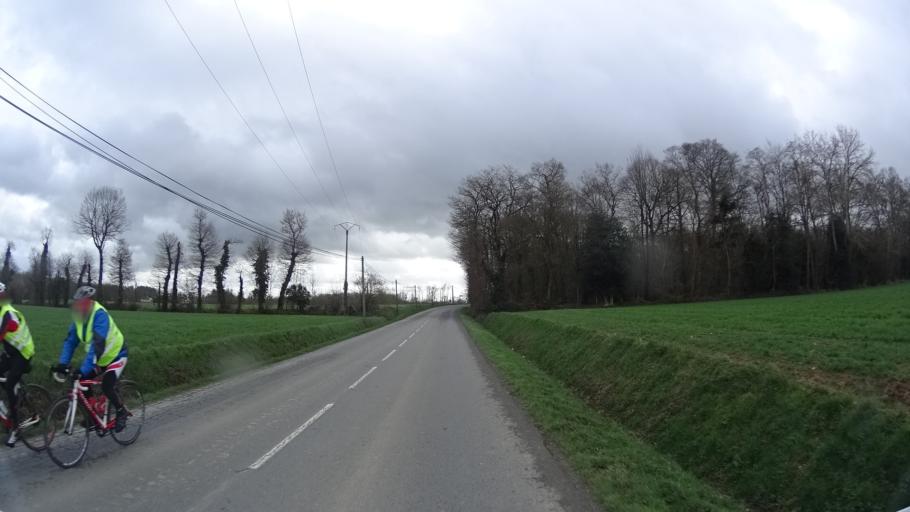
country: FR
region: Brittany
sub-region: Departement d'Ille-et-Vilaine
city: Saint-Gilles
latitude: 48.1791
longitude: -1.8488
